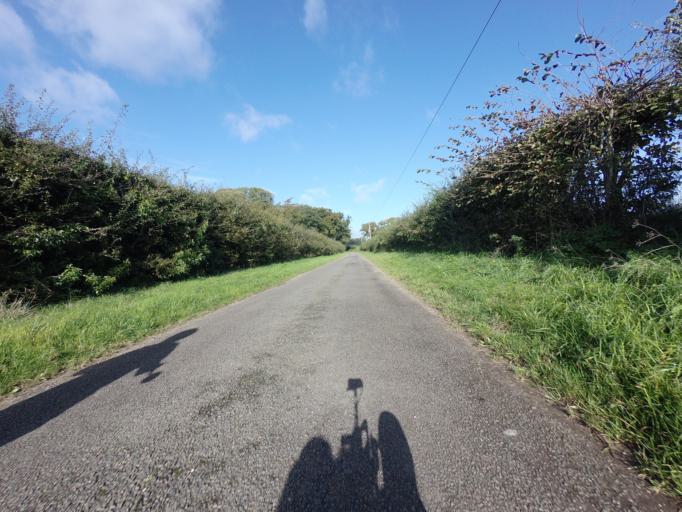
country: GB
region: England
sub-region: Norfolk
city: Dersingham
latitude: 52.8496
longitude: 0.6717
